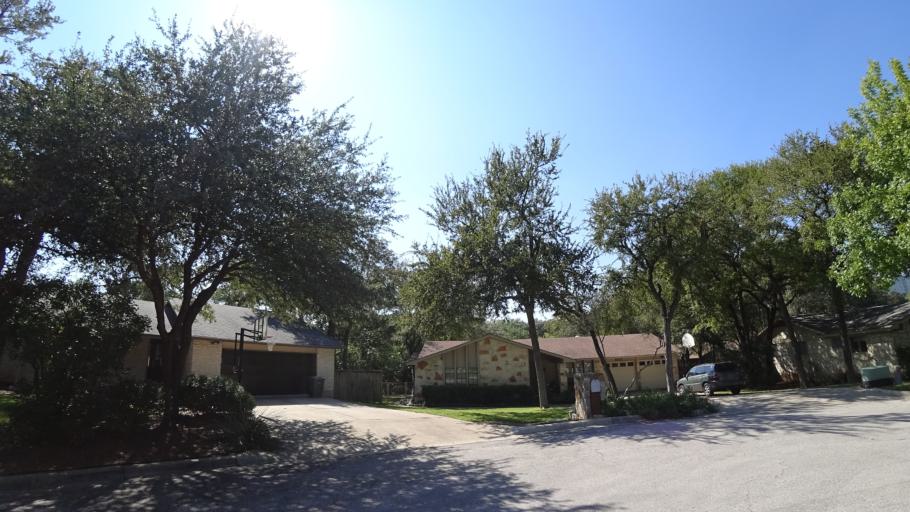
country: US
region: Texas
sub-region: Travis County
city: Rollingwood
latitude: 30.2487
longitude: -97.7939
